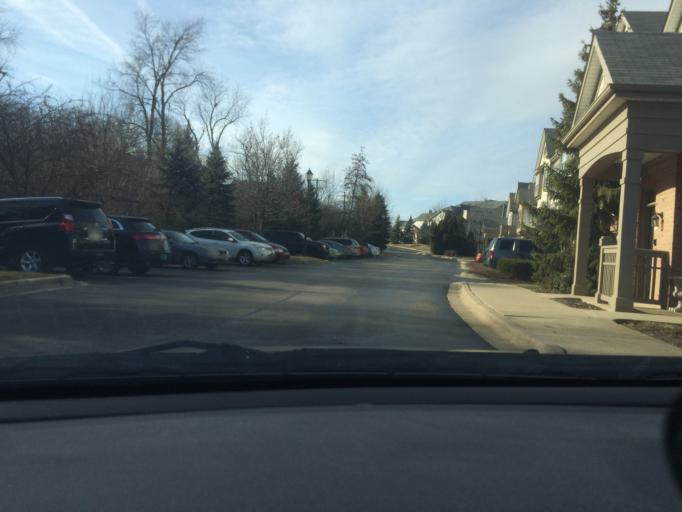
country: US
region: Illinois
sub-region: Kane County
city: Sleepy Hollow
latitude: 42.0758
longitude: -88.2905
